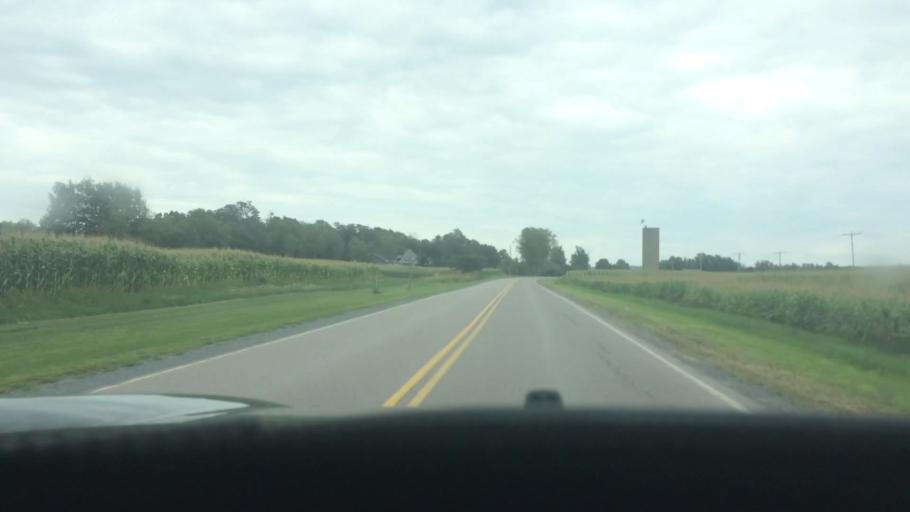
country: US
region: New York
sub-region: St. Lawrence County
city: Canton
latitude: 44.5421
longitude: -75.0891
